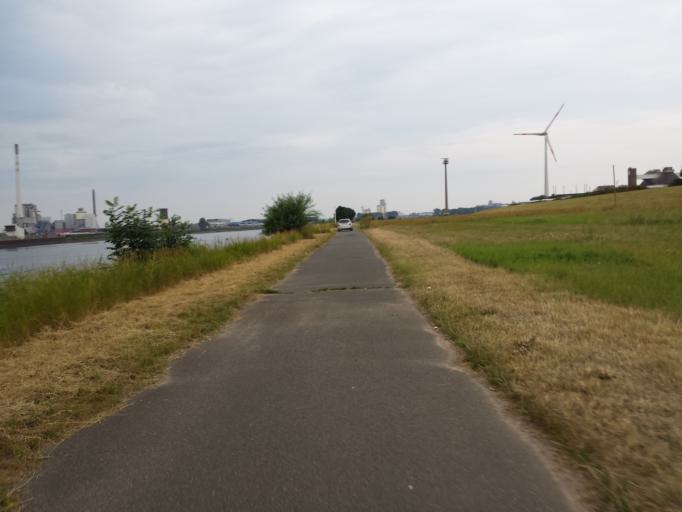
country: DE
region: Lower Saxony
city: Ritterhude
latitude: 53.1175
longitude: 8.7031
